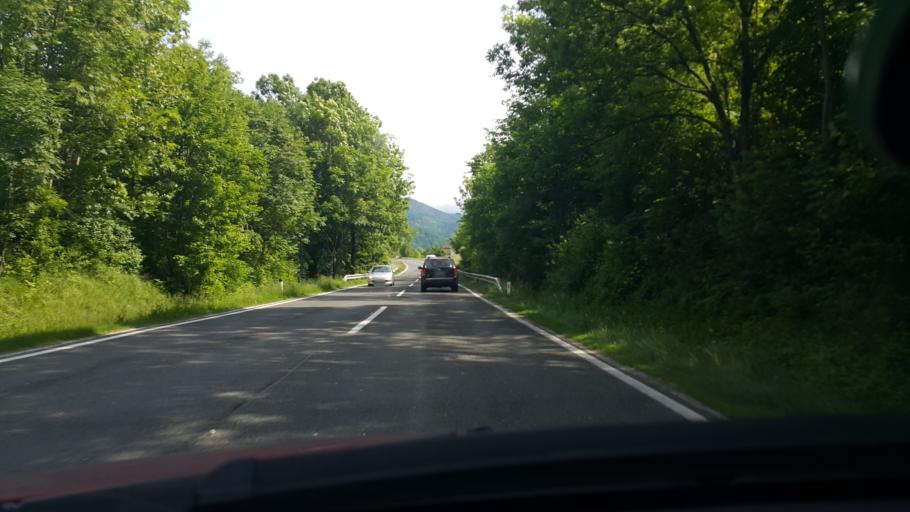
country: SI
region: Trzic
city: Bistrica pri Trzicu
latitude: 46.3385
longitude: 14.2841
